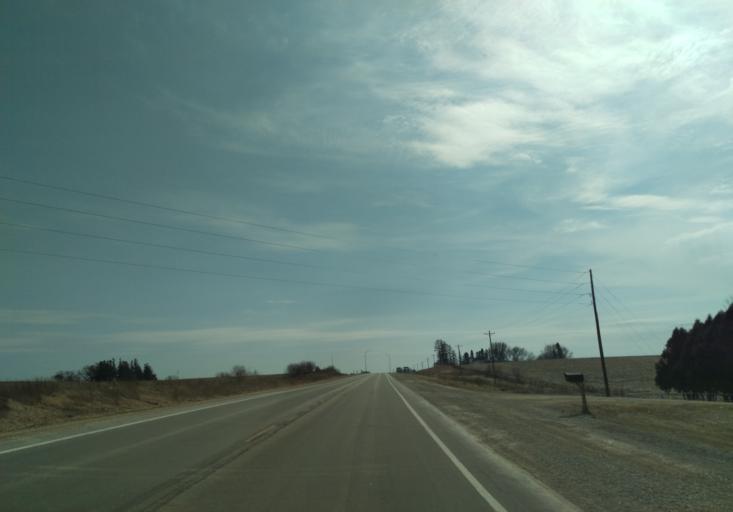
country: US
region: Iowa
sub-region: Winneshiek County
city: Decorah
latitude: 43.4471
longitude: -91.8625
